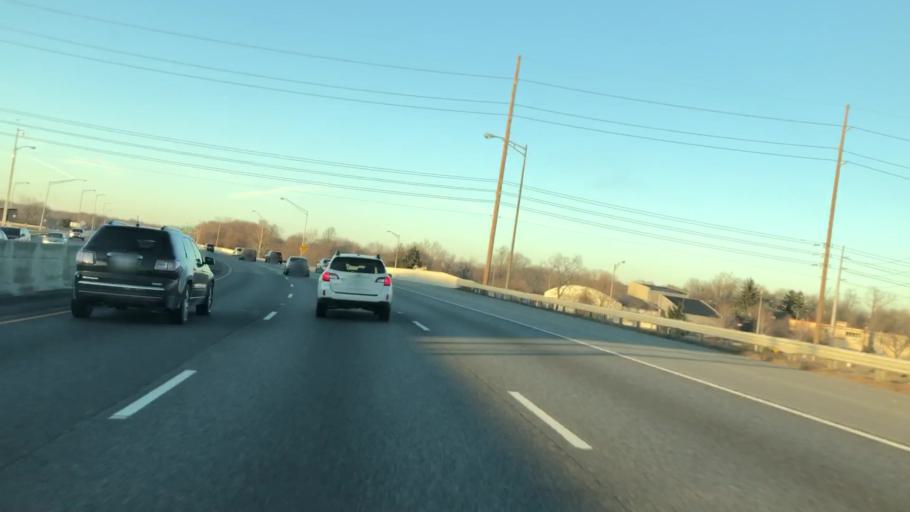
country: US
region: Indiana
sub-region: Marion County
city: Indianapolis
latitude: 39.7937
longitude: -86.1644
